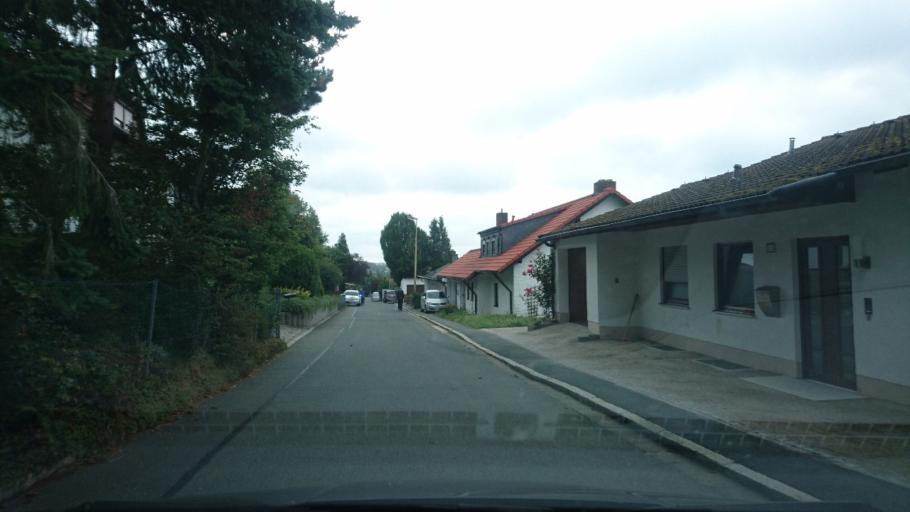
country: DE
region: Bavaria
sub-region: Upper Franconia
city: Naila
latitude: 50.3322
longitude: 11.6957
